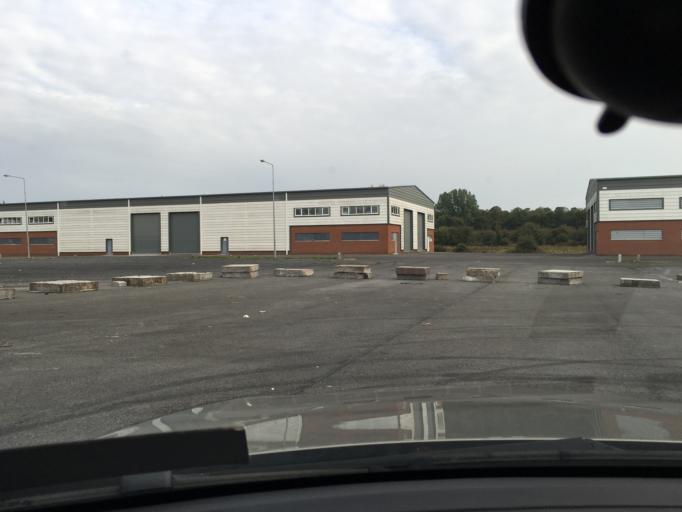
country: IE
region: Leinster
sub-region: An Longfort
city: Longford
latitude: 53.7200
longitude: -7.8037
